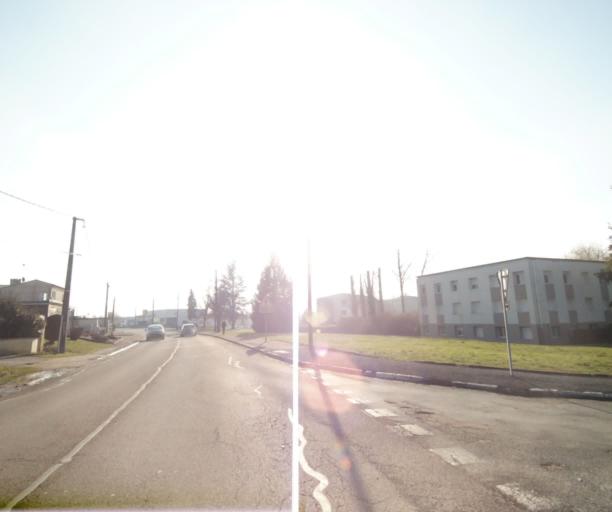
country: FR
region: Champagne-Ardenne
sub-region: Departement de la Haute-Marne
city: Wassy
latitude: 48.5042
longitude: 4.9434
